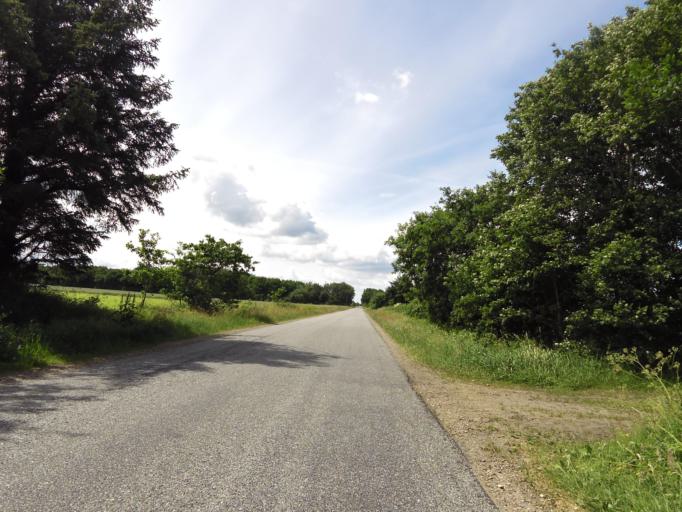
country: DK
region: South Denmark
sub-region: Esbjerg Kommune
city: Ribe
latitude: 55.2615
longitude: 8.8518
